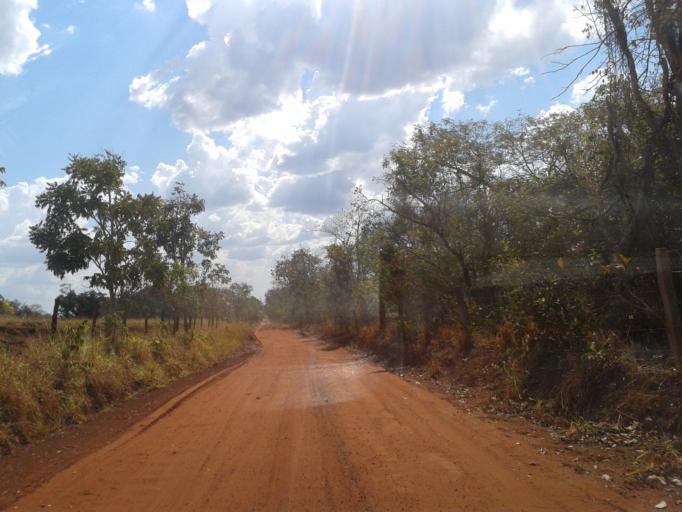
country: BR
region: Minas Gerais
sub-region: Santa Vitoria
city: Santa Vitoria
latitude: -19.1988
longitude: -49.9088
